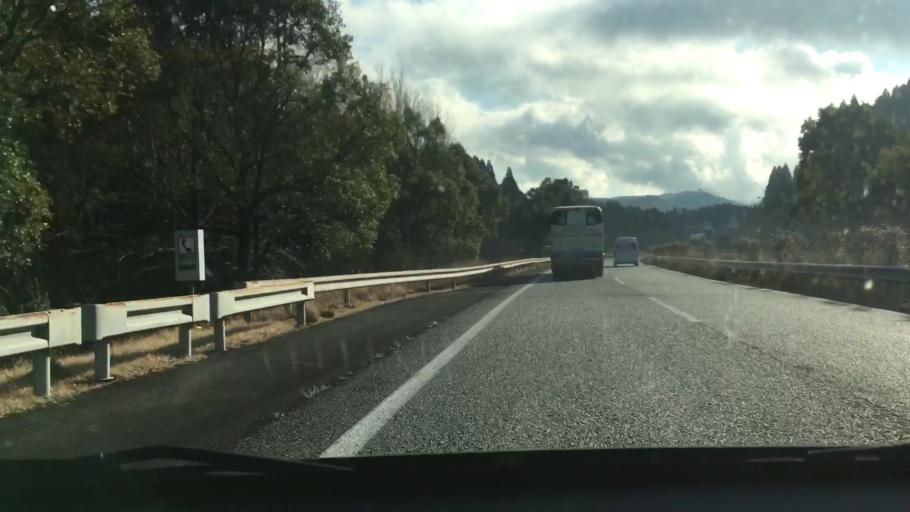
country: JP
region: Kagoshima
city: Okuchi-shinohara
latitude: 32.0314
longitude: 130.7980
